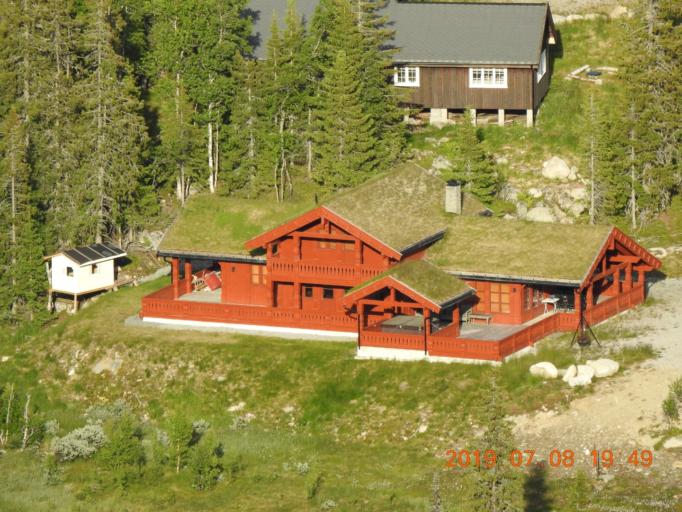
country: NO
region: Buskerud
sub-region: Nes
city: Nesbyen
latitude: 60.3492
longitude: 9.1713
